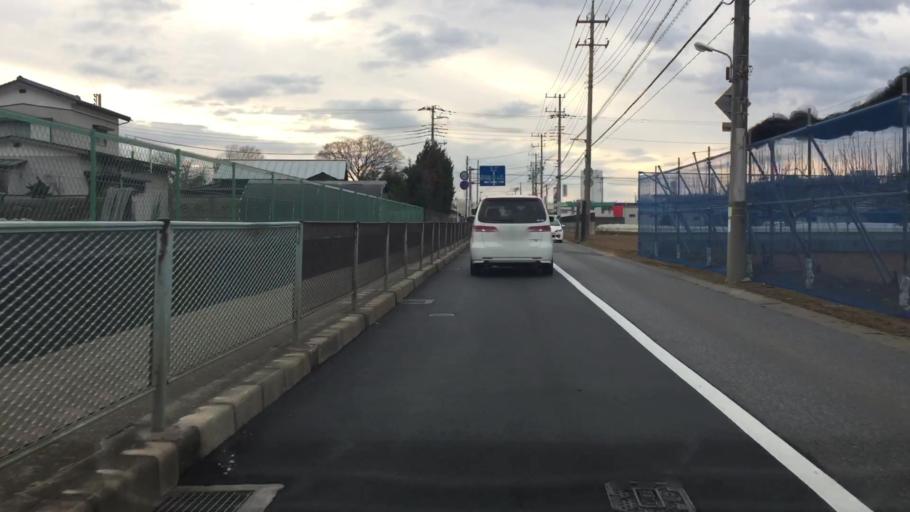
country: JP
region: Chiba
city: Kashiwa
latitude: 35.7848
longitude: 139.9833
